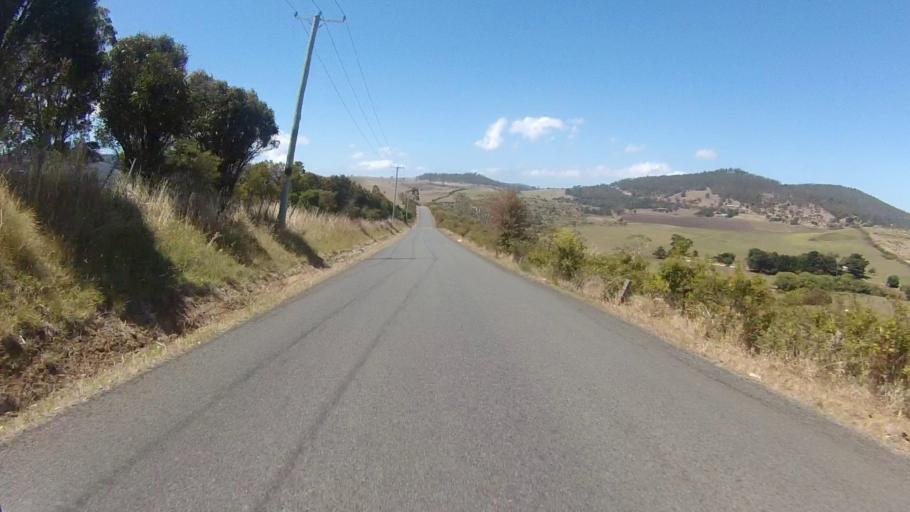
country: AU
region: Tasmania
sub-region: Sorell
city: Sorell
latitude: -42.7727
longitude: 147.5862
